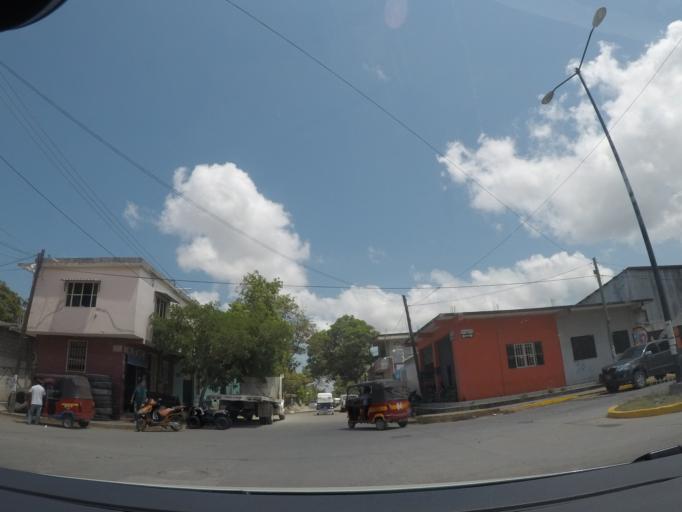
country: MX
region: Oaxaca
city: Juchitan de Zaragoza
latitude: 16.4362
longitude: -95.0161
